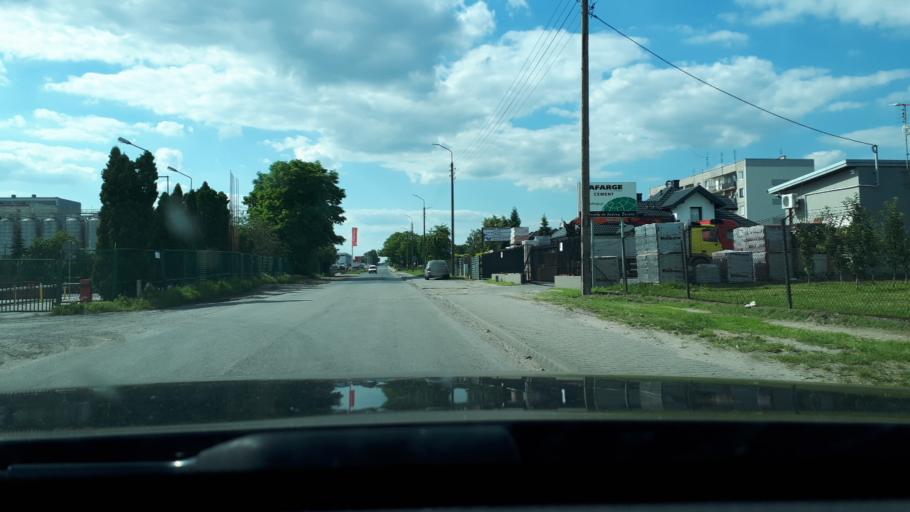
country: PL
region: Masovian Voivodeship
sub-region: Powiat grojecki
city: Warka
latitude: 51.8003
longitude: 21.1655
